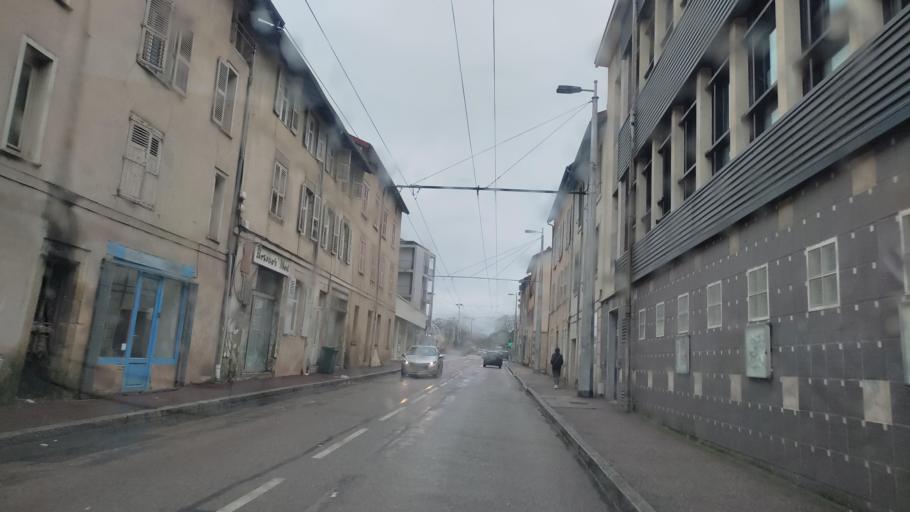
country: FR
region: Limousin
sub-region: Departement de la Haute-Vienne
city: Limoges
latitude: 45.8297
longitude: 1.2480
